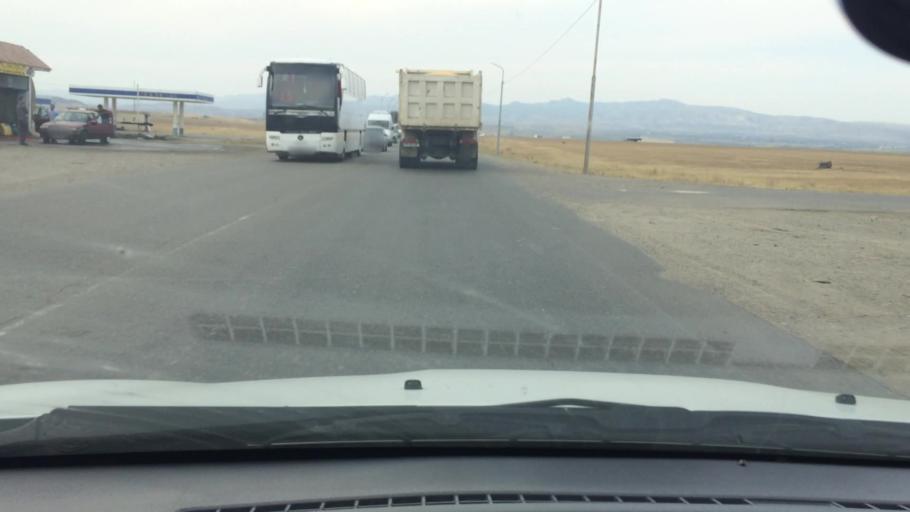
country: GE
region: Kvemo Kartli
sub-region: Marneuli
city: Marneuli
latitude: 41.5095
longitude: 44.7932
